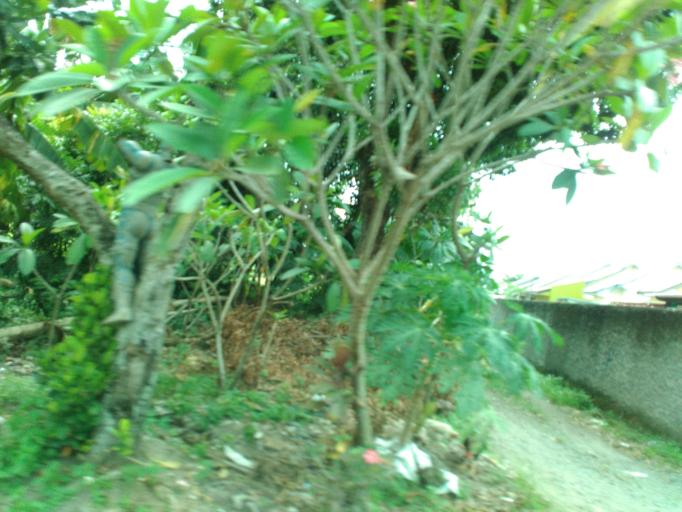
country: ID
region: Central Java
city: Klaten
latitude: -7.6859
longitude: 110.6316
